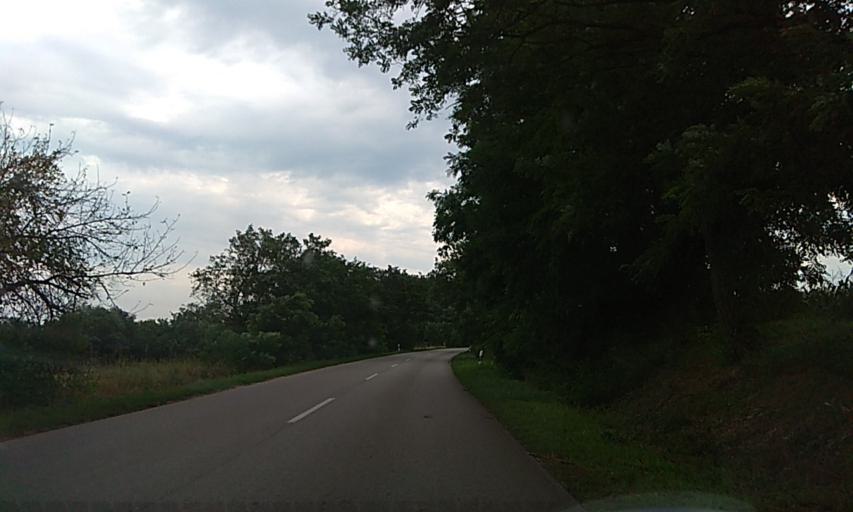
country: HU
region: Szabolcs-Szatmar-Bereg
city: Buj
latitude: 48.0812
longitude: 21.6407
